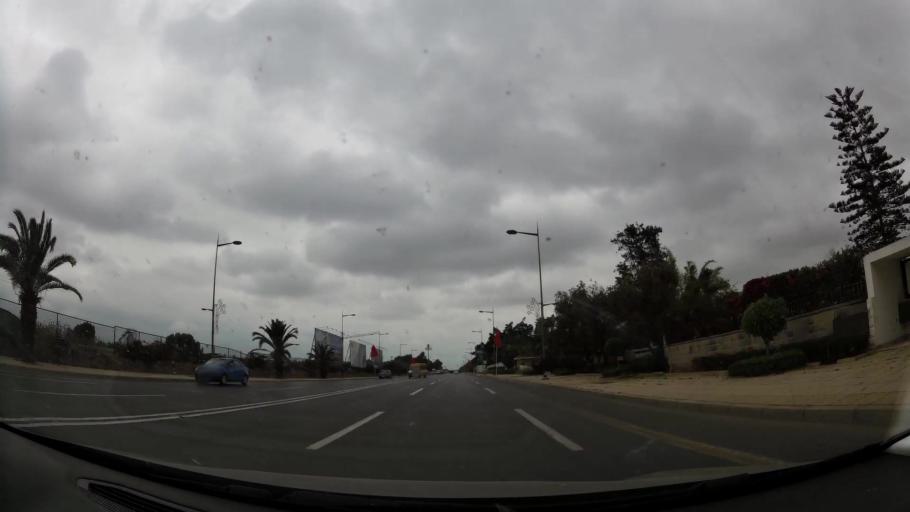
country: MA
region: Rabat-Sale-Zemmour-Zaer
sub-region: Rabat
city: Rabat
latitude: 33.9645
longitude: -6.8274
